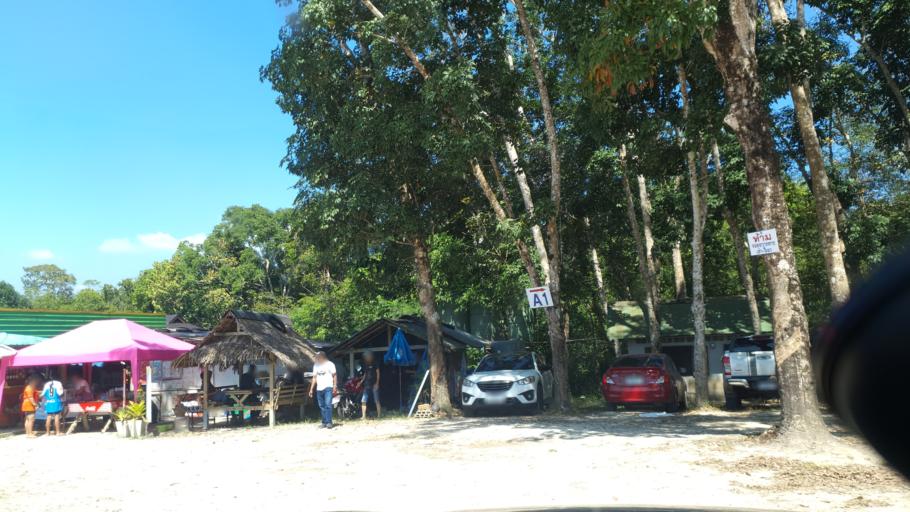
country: TH
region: Krabi
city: Khlong Thom
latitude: 7.9221
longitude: 99.2605
